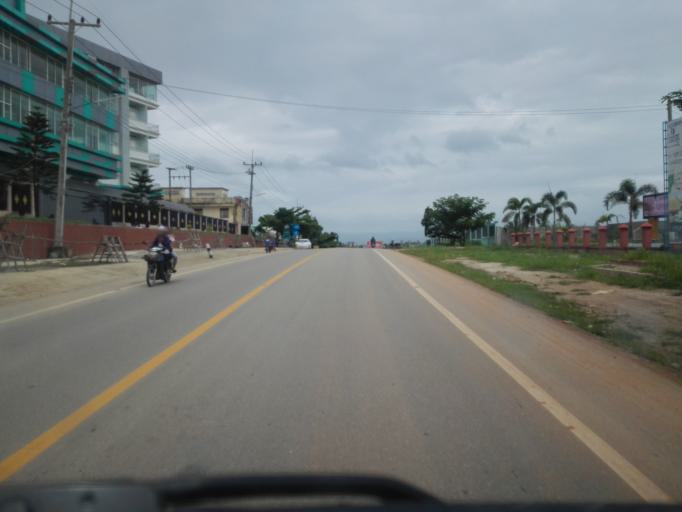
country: TH
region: Tak
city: Mae Sot
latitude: 16.6852
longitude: 98.4805
